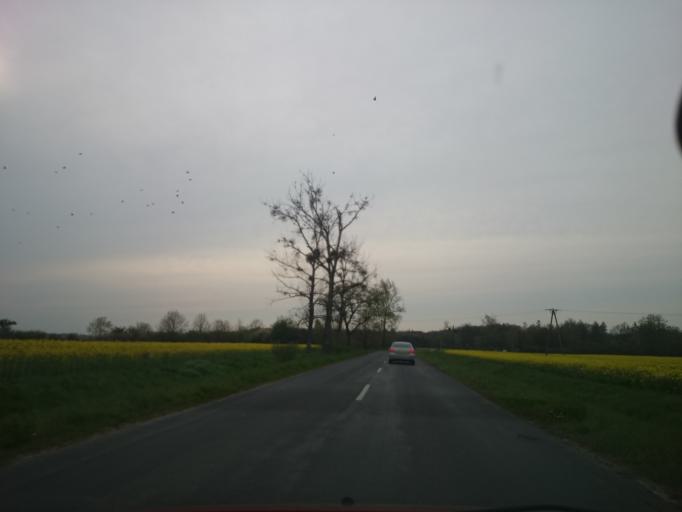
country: PL
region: Opole Voivodeship
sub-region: Powiat brzeski
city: Grodkow
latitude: 50.6587
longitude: 17.4300
